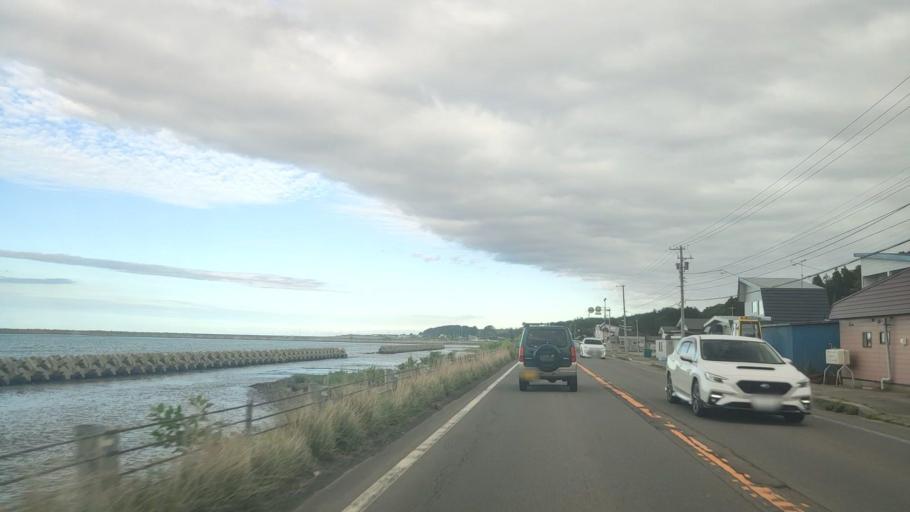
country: JP
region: Hokkaido
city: Nanae
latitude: 42.2289
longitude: 140.3333
